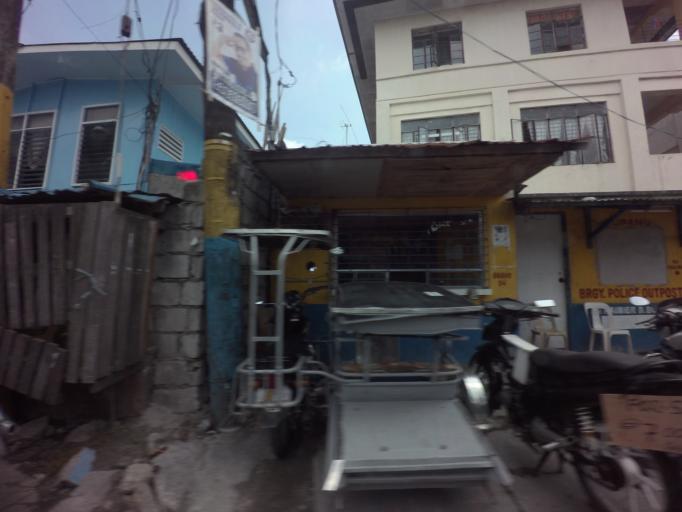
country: PH
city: Sambayanihan People's Village
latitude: 14.4301
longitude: 121.0500
